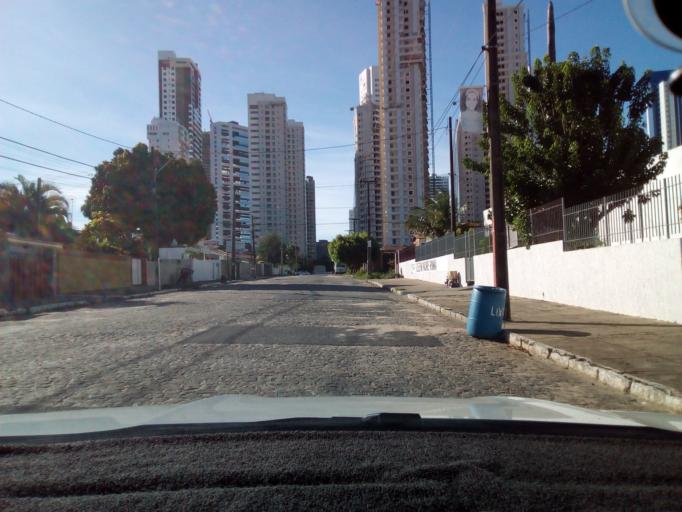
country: BR
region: Paraiba
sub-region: Joao Pessoa
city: Joao Pessoa
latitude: -7.1349
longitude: -34.8281
